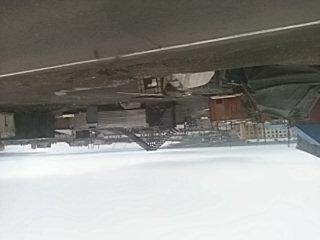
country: RU
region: Krasnoyarskiy
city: Dudinka
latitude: 69.4097
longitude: 86.1905
